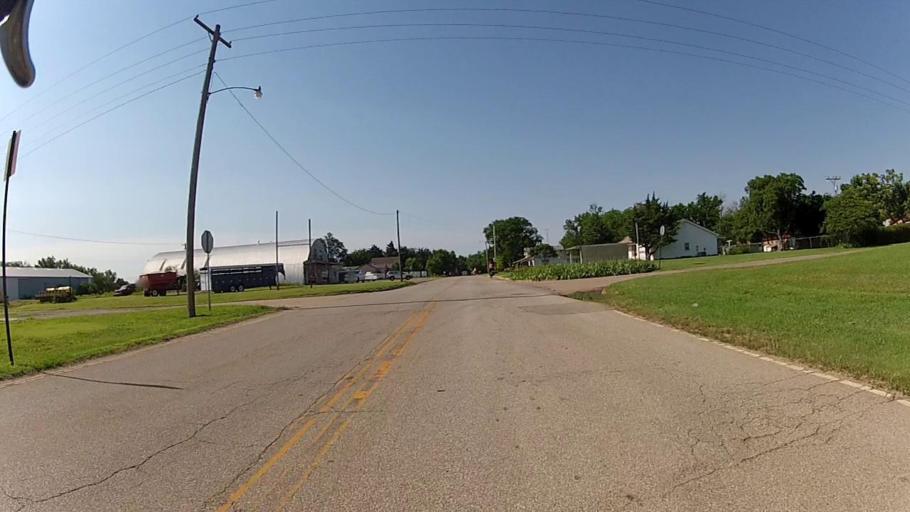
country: US
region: Kansas
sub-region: Sumner County
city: Caldwell
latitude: 37.0403
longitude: -97.6069
